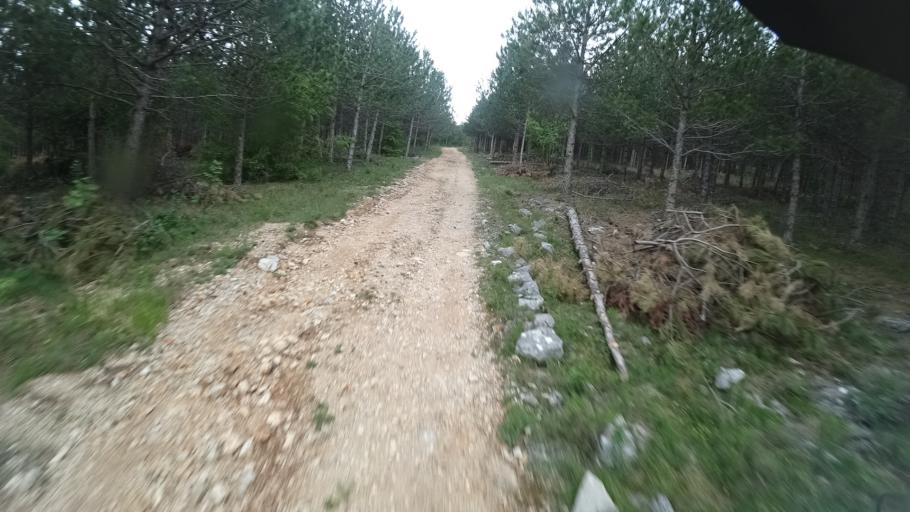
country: HR
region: Sibensko-Kniniska
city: Knin
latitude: 43.9866
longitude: 16.3387
